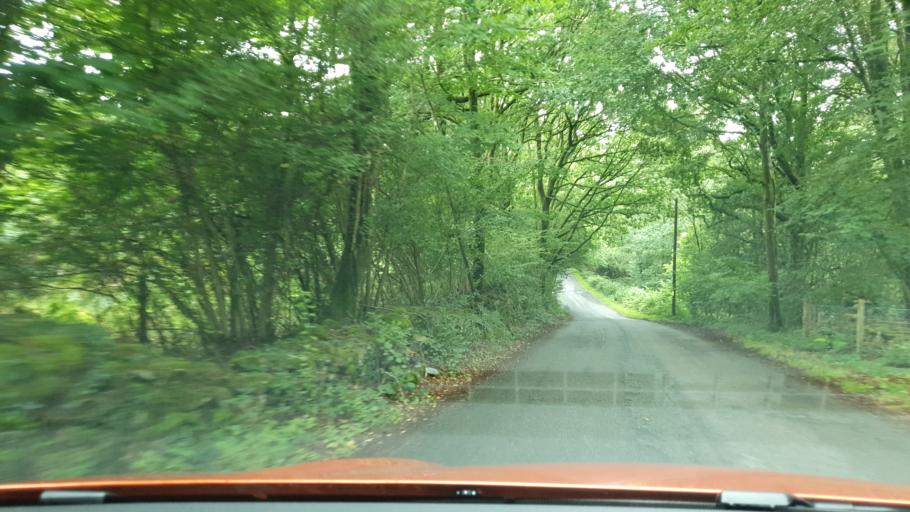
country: GB
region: England
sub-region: Cumbria
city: Grange-over-Sands
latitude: 54.2682
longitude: -2.9854
